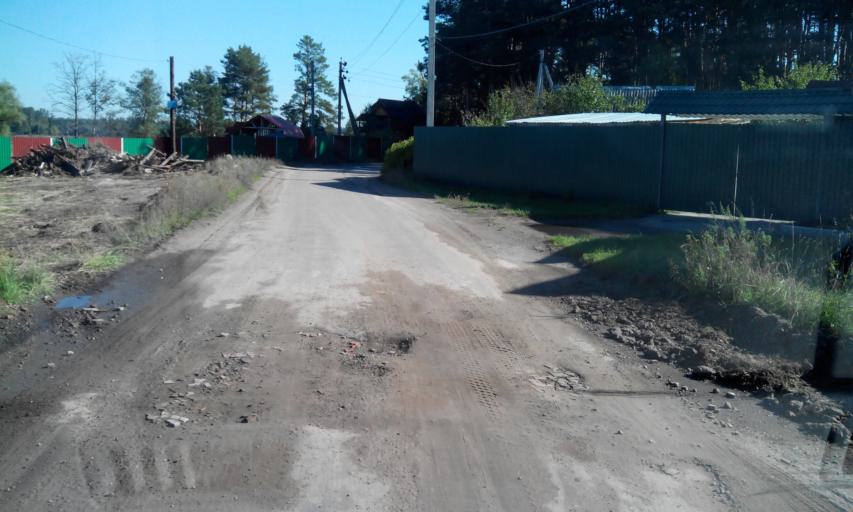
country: RU
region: Penza
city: Zarechnyy
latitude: 53.2729
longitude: 45.1308
